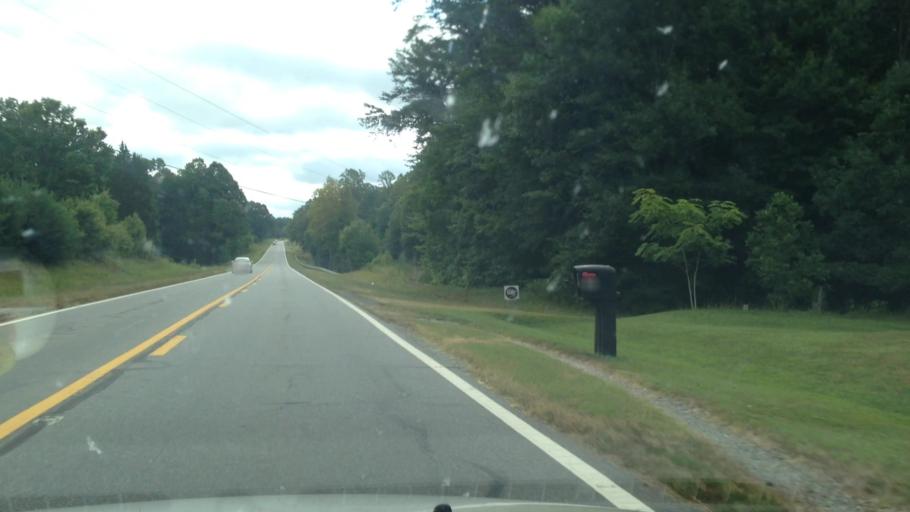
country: US
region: North Carolina
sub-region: Rockingham County
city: Wentworth
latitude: 36.3765
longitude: -79.8471
